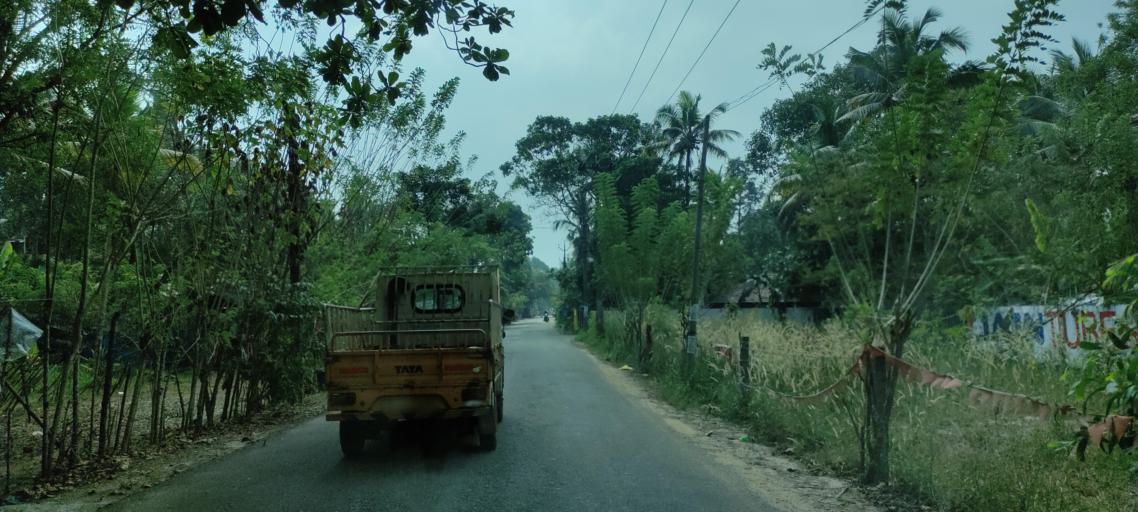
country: IN
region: Kerala
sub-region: Alappuzha
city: Shertallai
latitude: 9.6165
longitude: 76.3477
